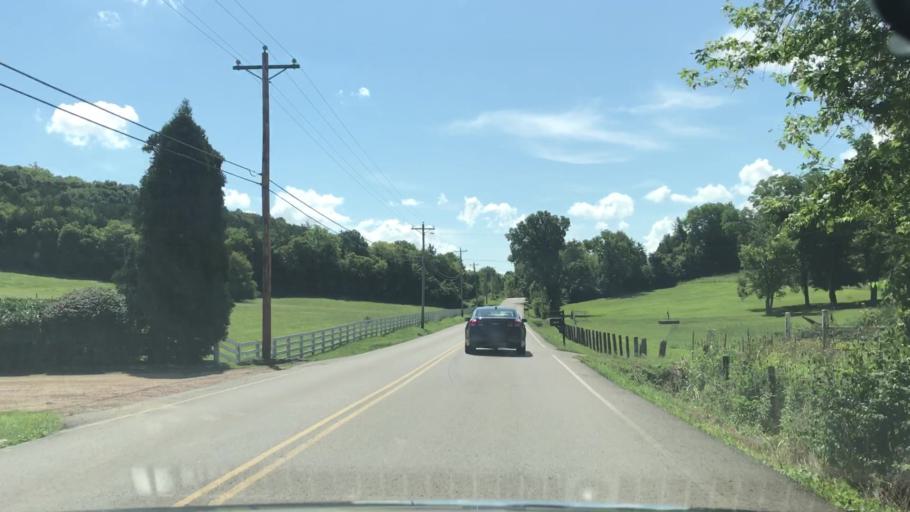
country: US
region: Tennessee
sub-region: Williamson County
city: Franklin
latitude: 35.9582
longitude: -86.8512
